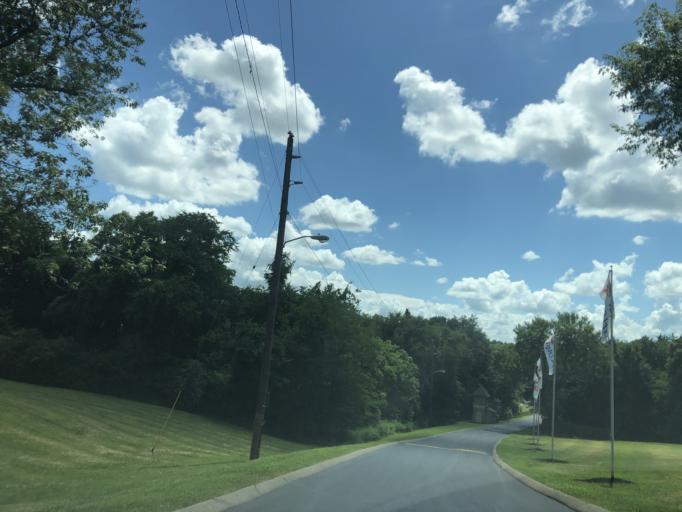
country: US
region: Tennessee
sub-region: Davidson County
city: Oak Hill
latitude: 36.0709
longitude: -86.7177
